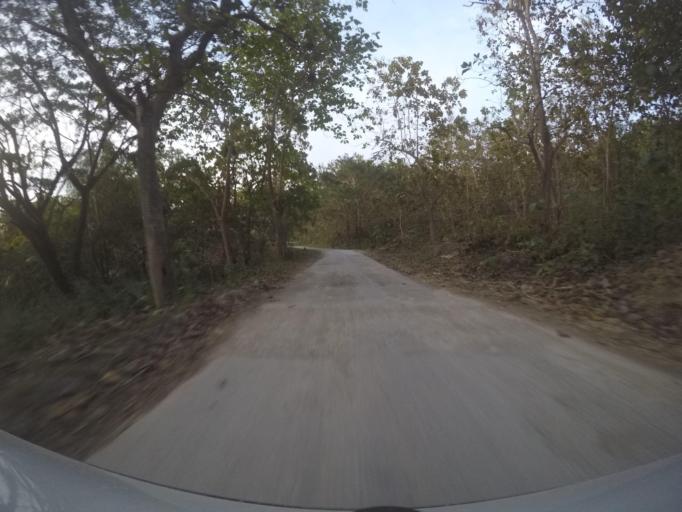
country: TL
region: Viqueque
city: Viqueque
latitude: -8.9051
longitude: 126.3923
